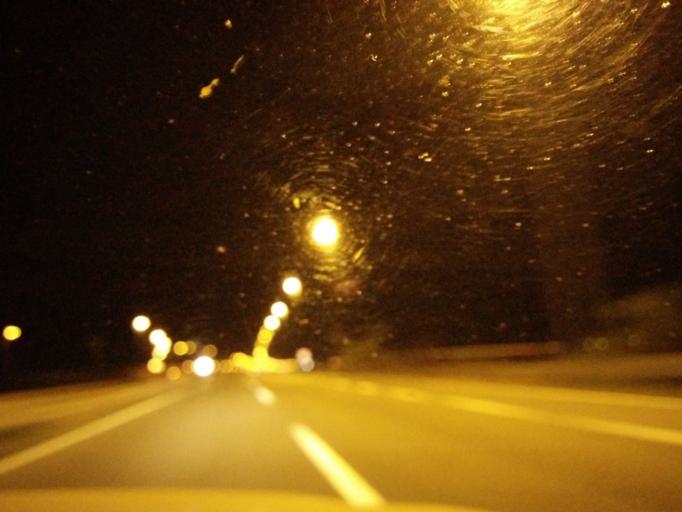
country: RS
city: Dobanovci
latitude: 44.8369
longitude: 20.2446
